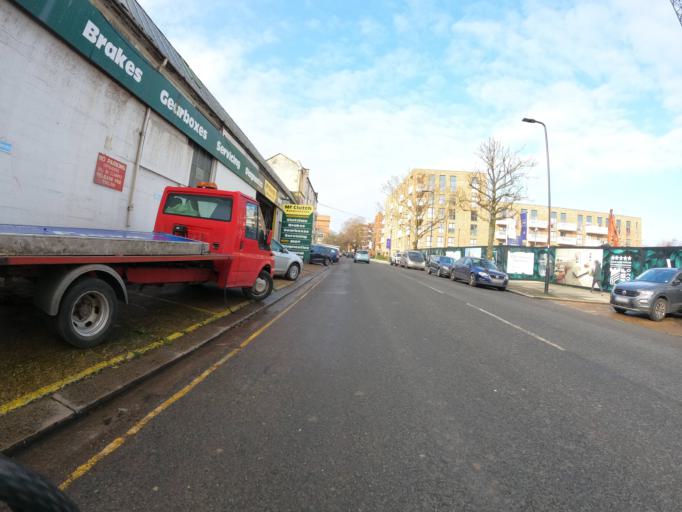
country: GB
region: England
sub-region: Greater London
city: Acton
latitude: 51.5018
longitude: -0.2784
